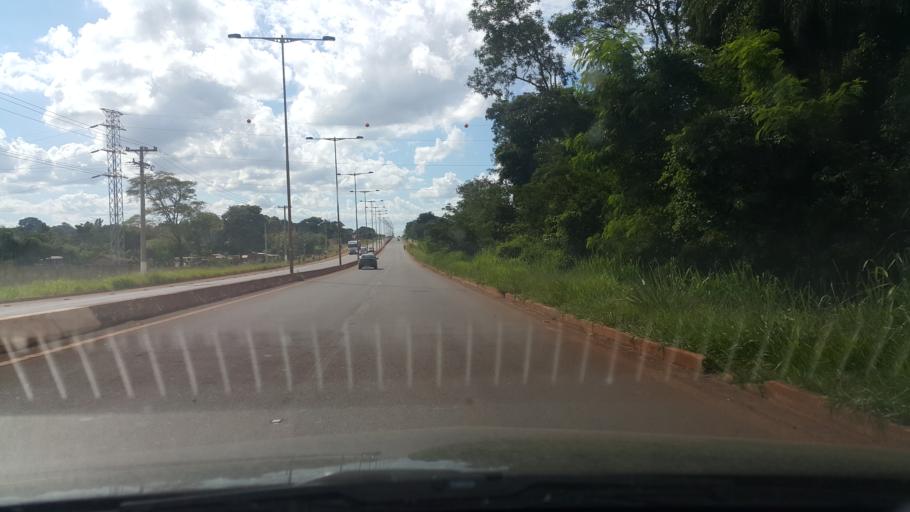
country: BR
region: Mato Grosso do Sul
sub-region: Dourados
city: Dourados
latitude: -22.1925
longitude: -54.8165
